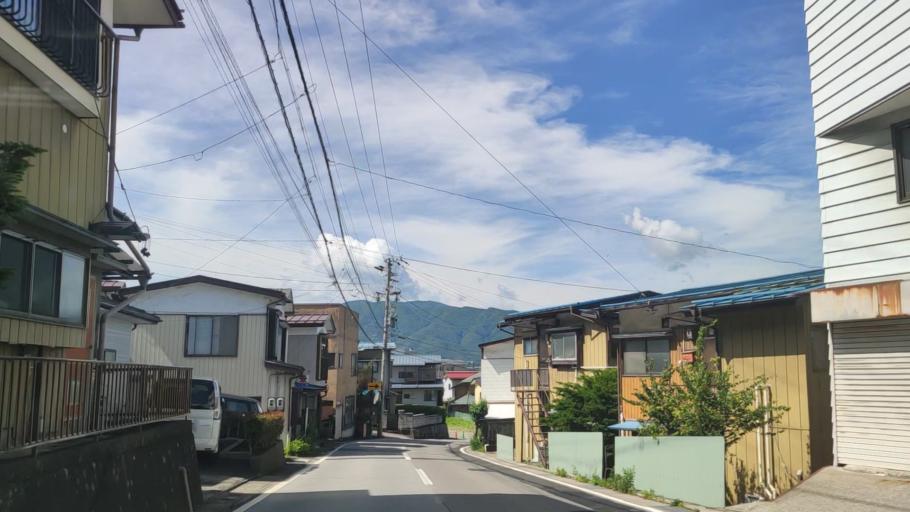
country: JP
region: Nagano
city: Suwa
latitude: 36.0413
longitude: 138.1260
